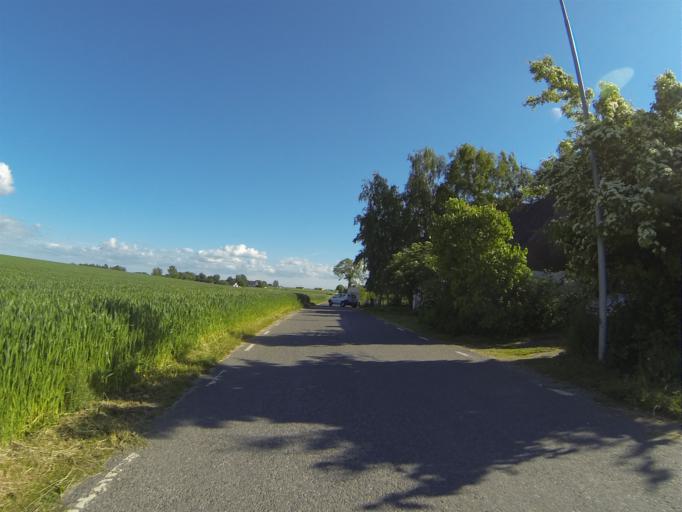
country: SE
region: Skane
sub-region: Staffanstorps Kommun
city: Staffanstorp
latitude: 55.6713
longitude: 13.2009
